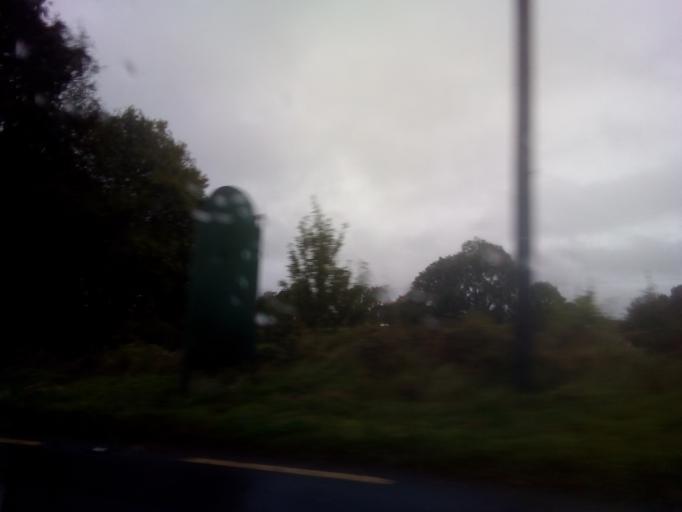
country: IE
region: Connaught
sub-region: Roscommon
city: Castlerea
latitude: 53.8403
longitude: -8.3846
